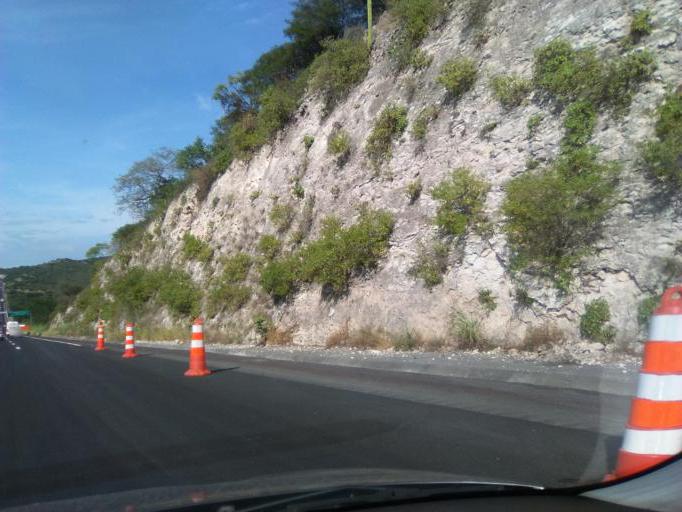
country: MX
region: Morelos
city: Tilzapotla
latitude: 18.4484
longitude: -99.1738
